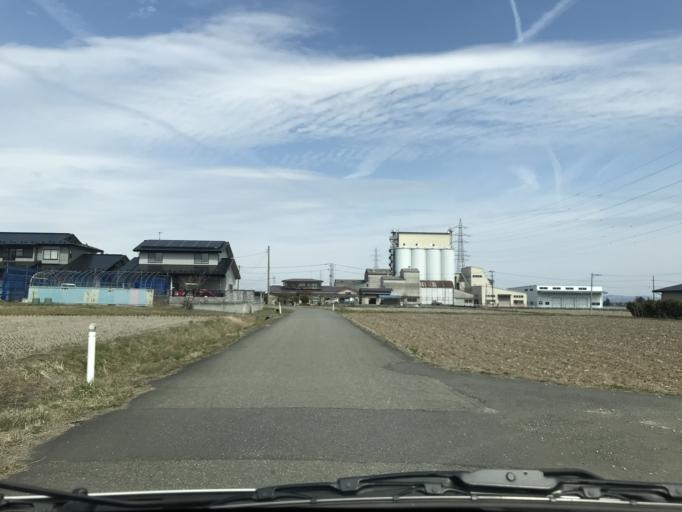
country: JP
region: Iwate
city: Mizusawa
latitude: 39.1383
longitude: 141.0832
